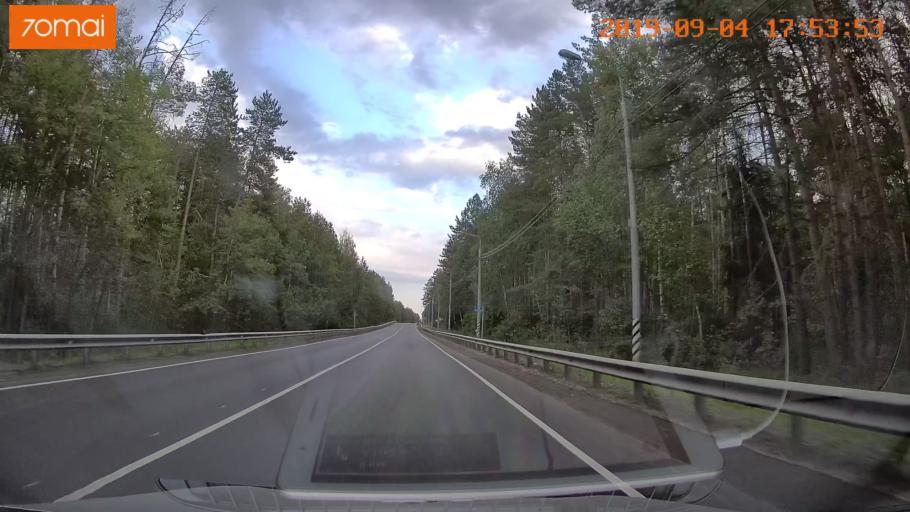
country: RU
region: Moskovskaya
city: Imeni Tsyurupy
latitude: 55.5136
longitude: 38.7312
